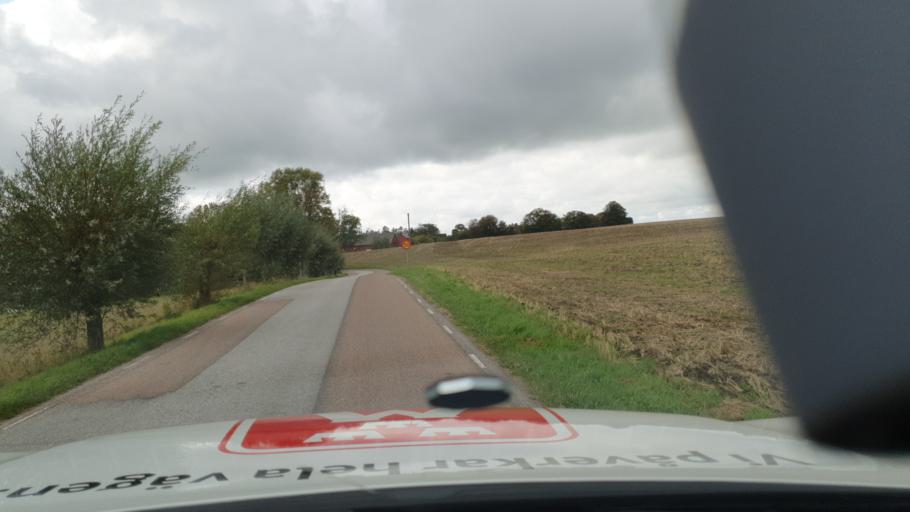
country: SE
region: Skane
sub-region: Trelleborgs Kommun
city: Trelleborg
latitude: 55.4553
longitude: 13.1648
